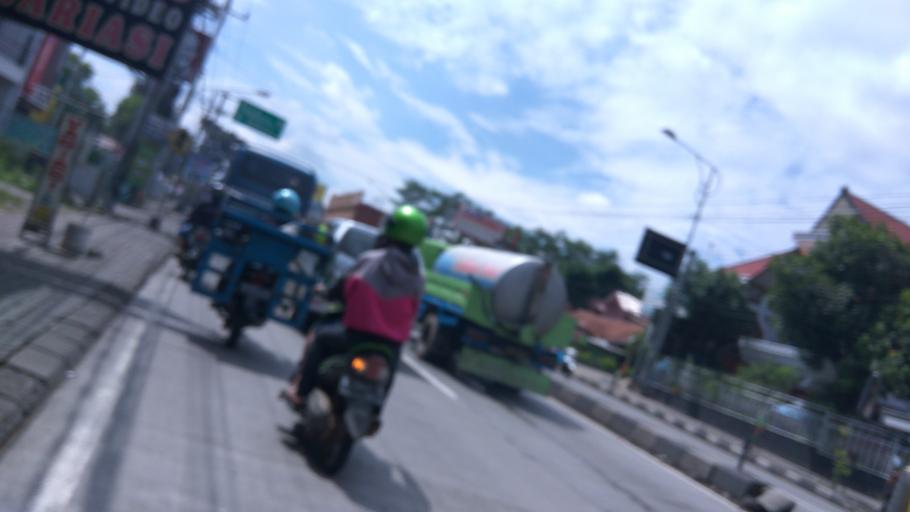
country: ID
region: Central Java
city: Ungaran
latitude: -7.1459
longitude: 110.4071
